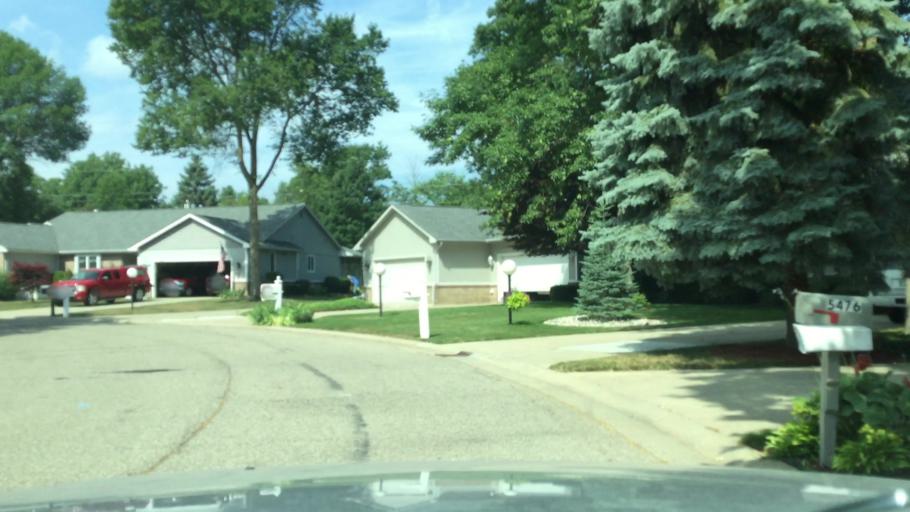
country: US
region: Michigan
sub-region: Genesee County
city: Flushing
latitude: 43.0581
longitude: -83.7906
